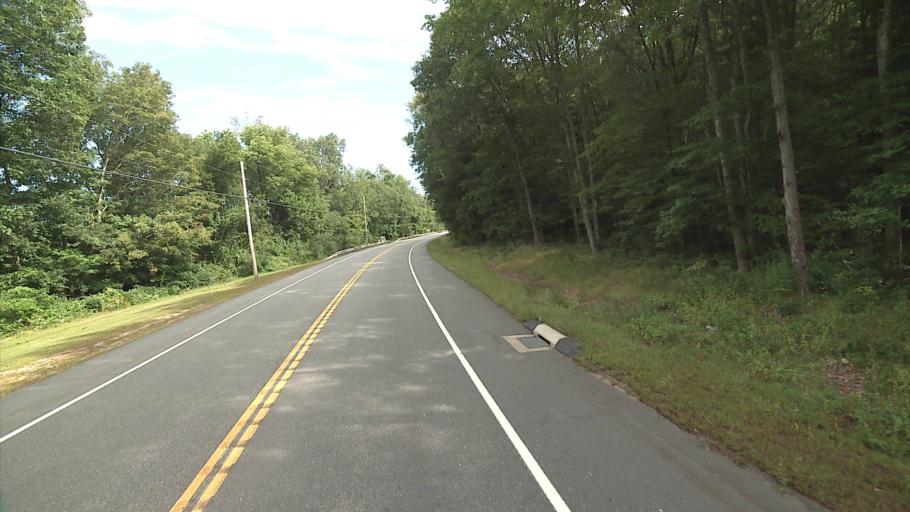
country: US
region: Connecticut
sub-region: Tolland County
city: South Coventry
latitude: 41.8273
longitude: -72.3100
